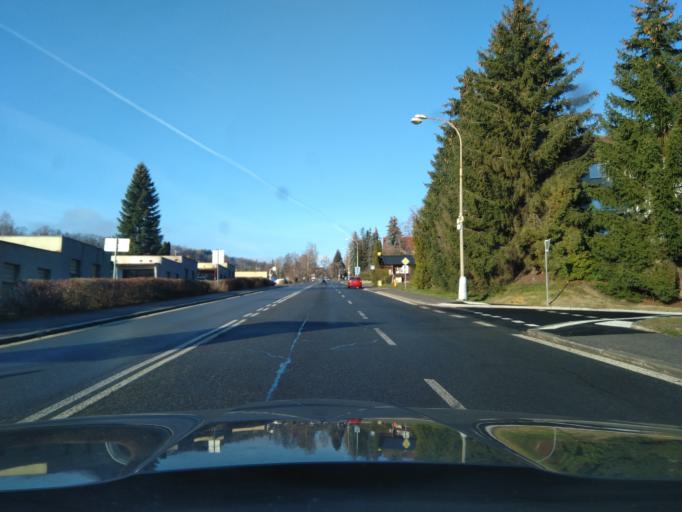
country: CZ
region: Jihocesky
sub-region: Okres Prachatice
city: Vimperk
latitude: 49.0586
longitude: 13.7827
